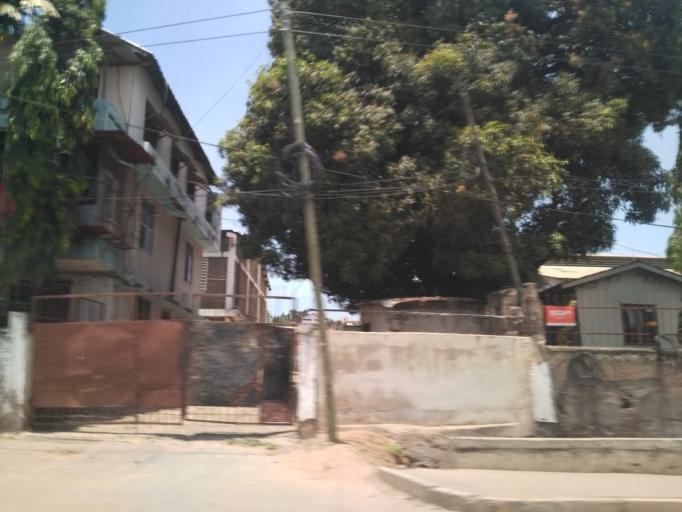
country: TZ
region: Mwanza
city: Mwanza
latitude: -2.5350
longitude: 32.9033
